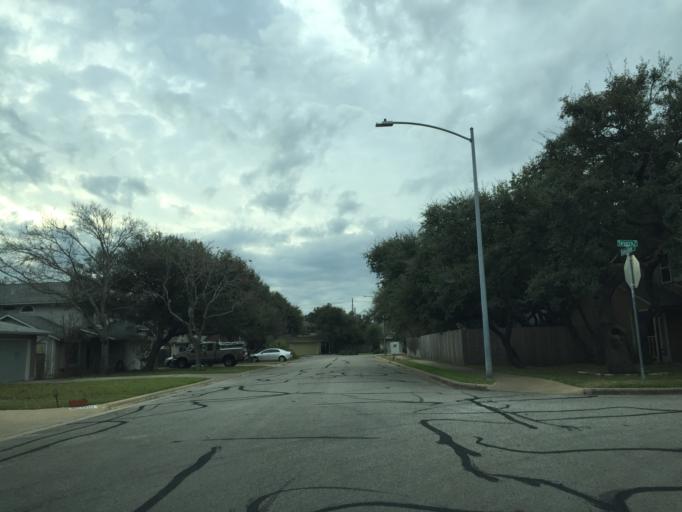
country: US
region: Texas
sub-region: Williamson County
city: Jollyville
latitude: 30.4467
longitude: -97.7508
